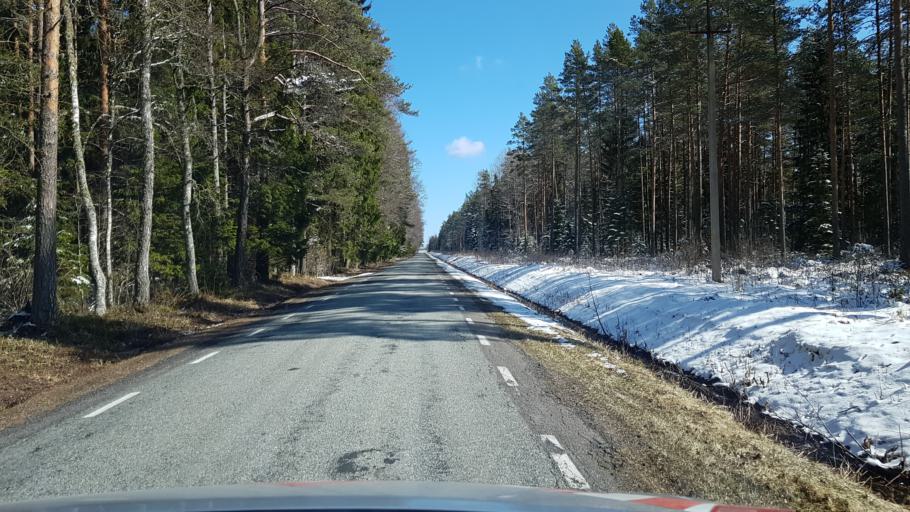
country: EE
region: Laeaene-Virumaa
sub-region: Kadrina vald
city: Kadrina
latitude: 59.5243
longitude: 26.0103
